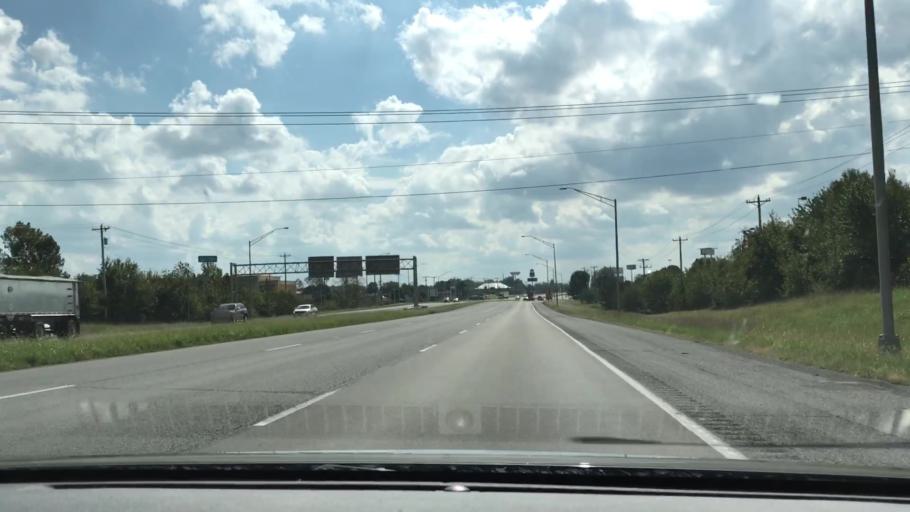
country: US
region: Kentucky
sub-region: Christian County
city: Oak Grove
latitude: 36.7002
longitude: -87.4544
